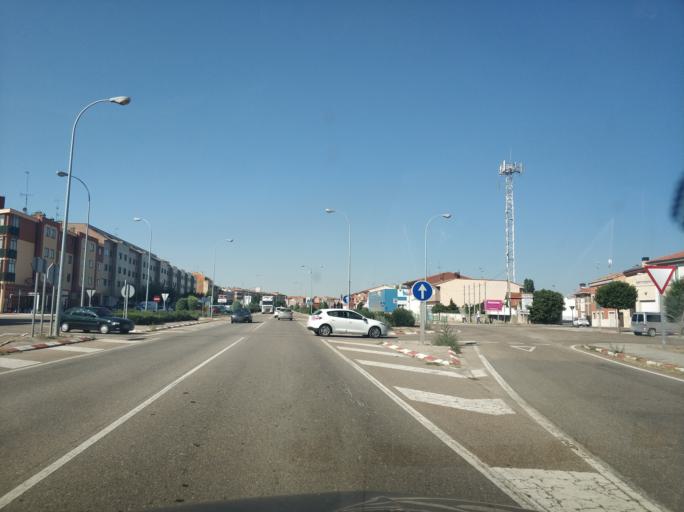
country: ES
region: Castille and Leon
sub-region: Provincia de Valladolid
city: Penafiel
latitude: 41.5998
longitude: -4.1210
